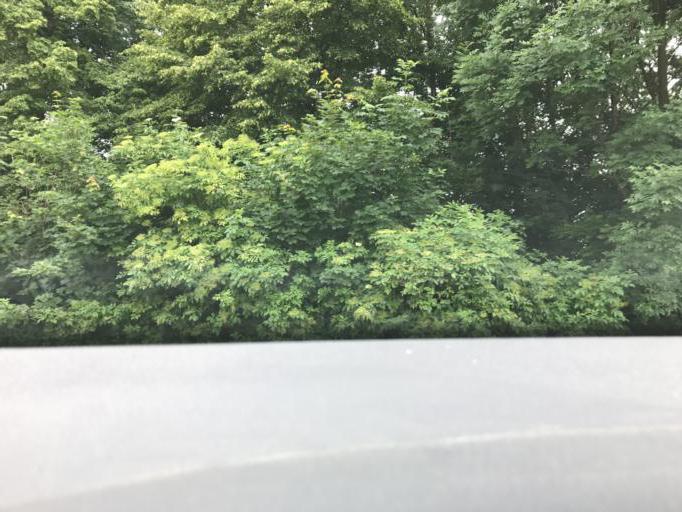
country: PL
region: Pomeranian Voivodeship
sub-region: Powiat gdanski
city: Suchy Dab
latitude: 54.2469
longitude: 18.7225
